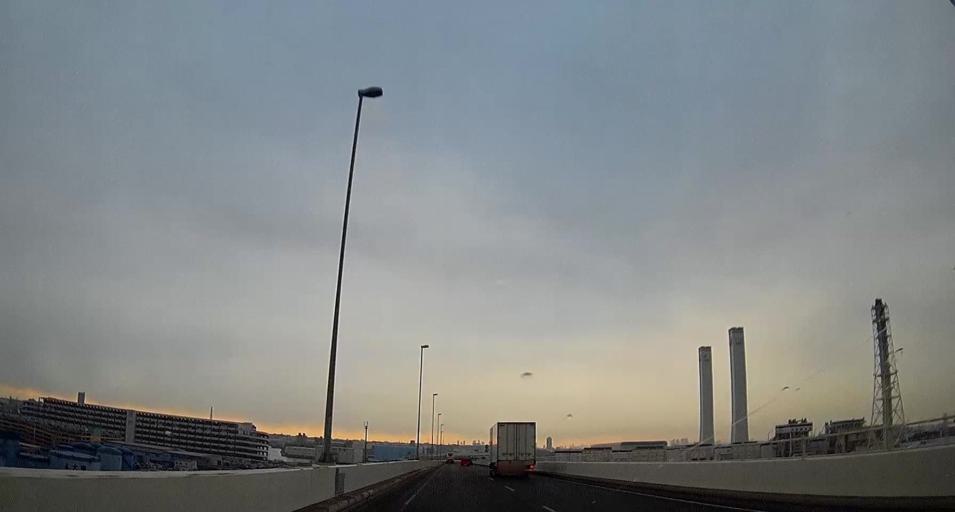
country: JP
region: Kanagawa
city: Yokohama
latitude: 35.4688
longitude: 139.6766
